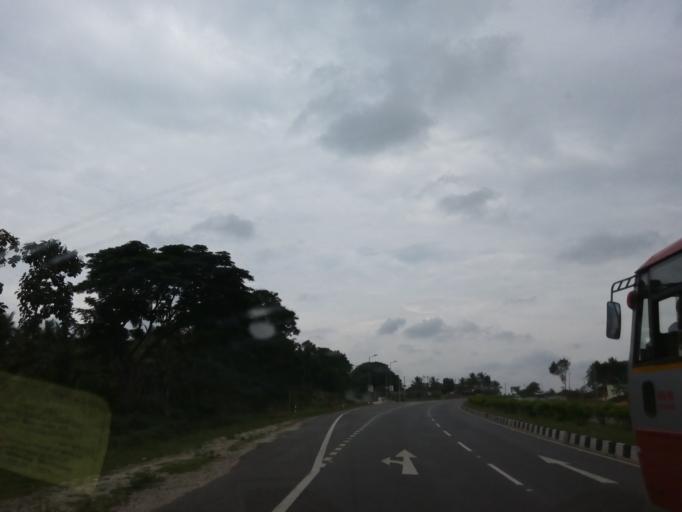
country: IN
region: Karnataka
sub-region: Hassan
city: Channarayapatna
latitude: 12.9438
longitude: 76.3398
